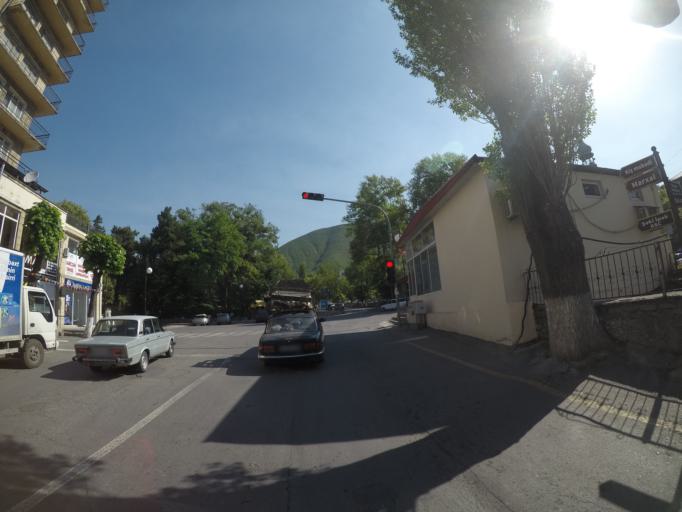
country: AZ
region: Shaki City
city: Sheki
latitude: 41.2023
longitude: 47.1803
